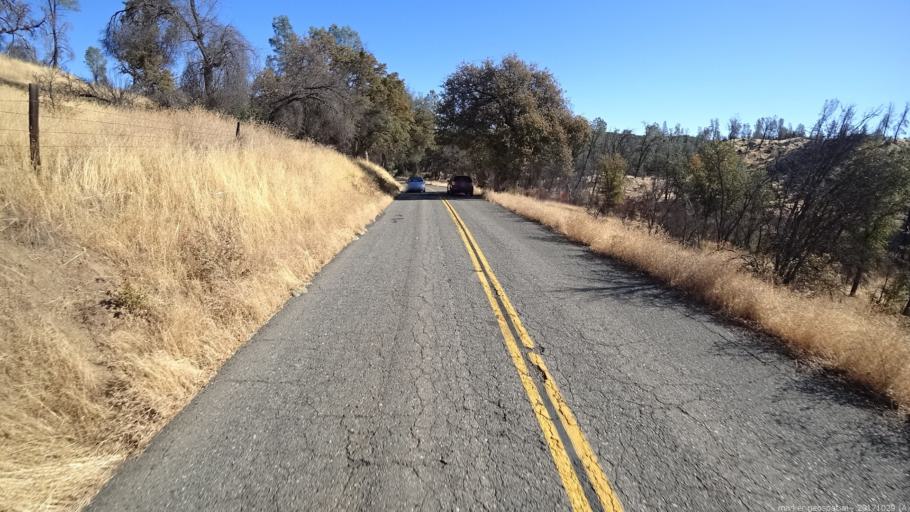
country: US
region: California
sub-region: Trinity County
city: Lewiston
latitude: 40.4235
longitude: -122.7341
